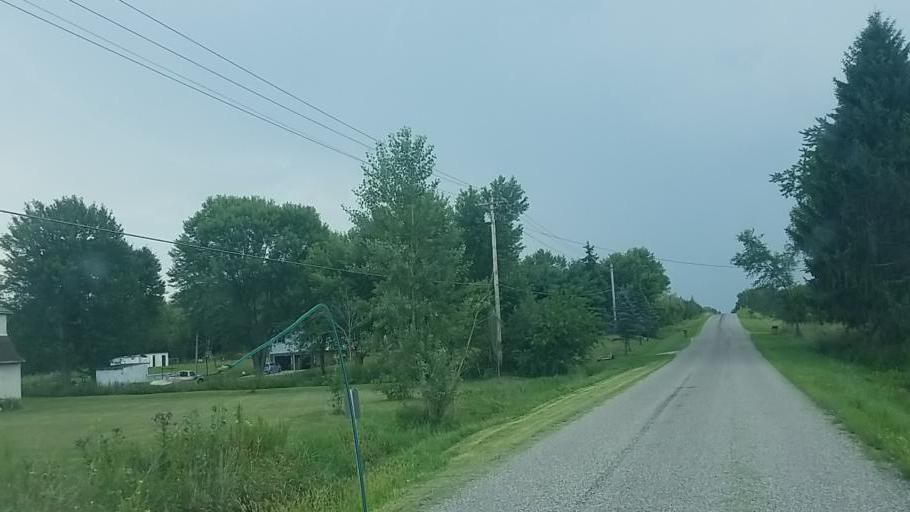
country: US
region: Ohio
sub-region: Medina County
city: Lodi
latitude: 40.9999
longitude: -82.0057
